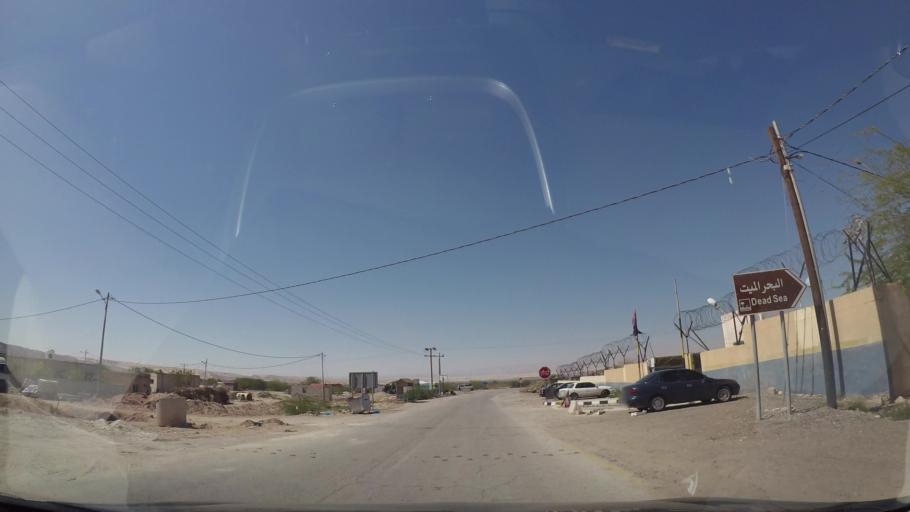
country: JO
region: Karak
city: Safi
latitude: 30.9163
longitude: 35.4591
